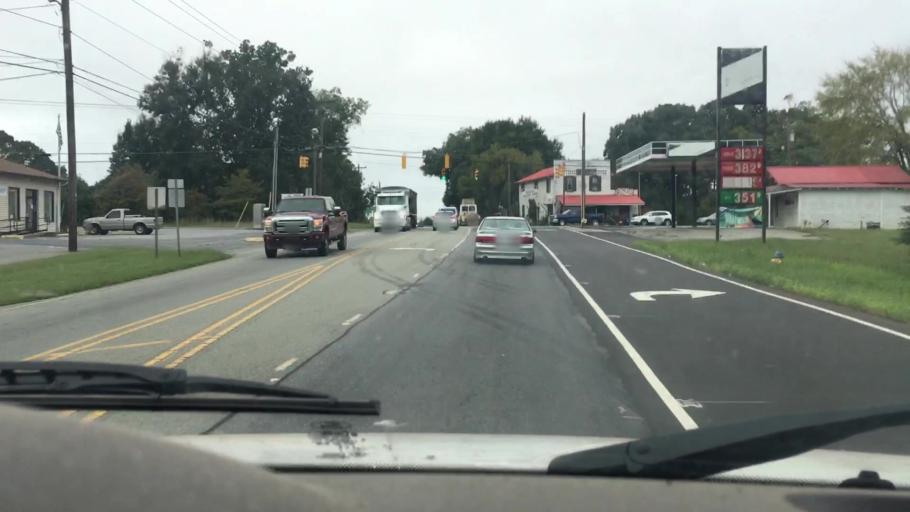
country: US
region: North Carolina
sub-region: Catawba County
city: Lake Norman of Catawba
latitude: 35.5895
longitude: -80.9769
